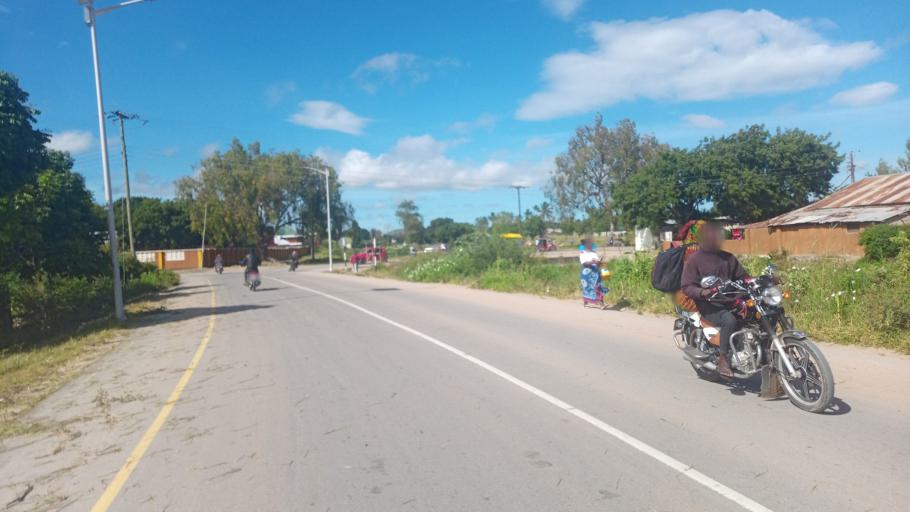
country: TZ
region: Dodoma
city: Dodoma
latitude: -6.1818
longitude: 35.7378
